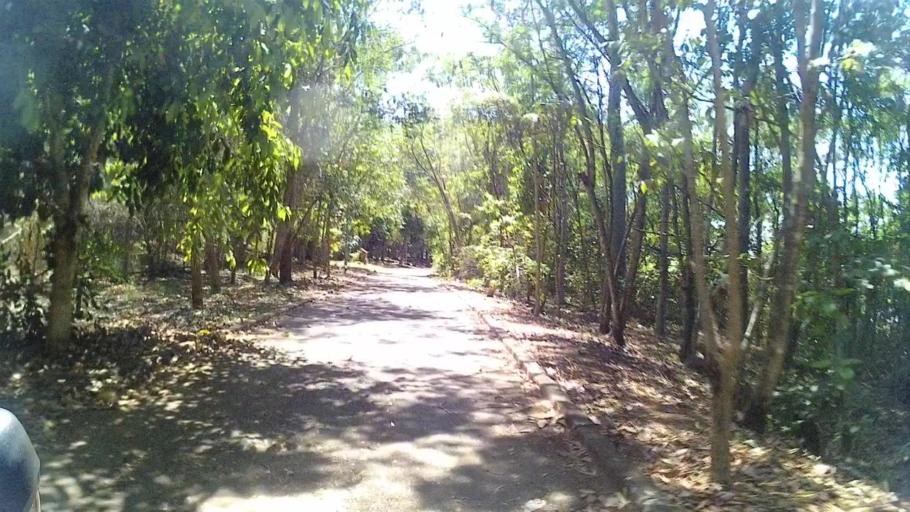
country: BR
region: Federal District
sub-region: Brasilia
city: Brasilia
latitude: -15.7294
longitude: -47.8895
